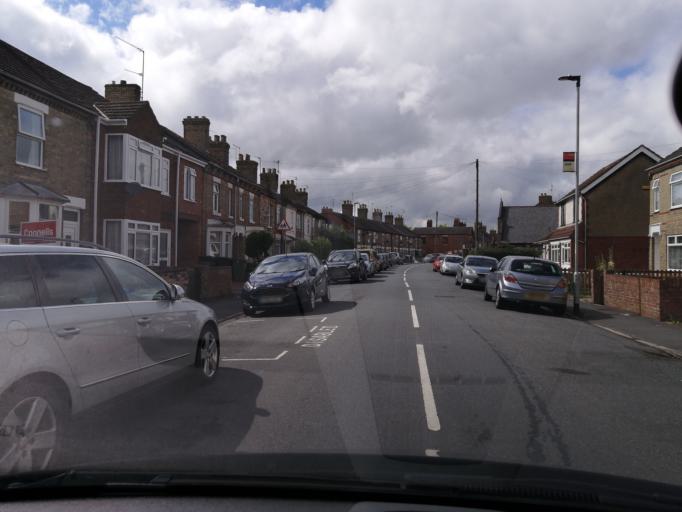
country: GB
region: England
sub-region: Peterborough
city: Peterborough
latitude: 52.5619
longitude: -0.2535
